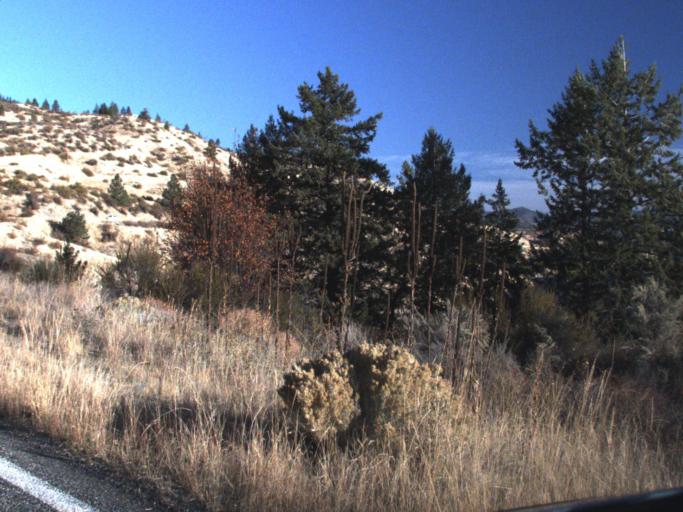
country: US
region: Washington
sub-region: Okanogan County
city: Coulee Dam
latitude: 47.9700
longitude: -118.6998
